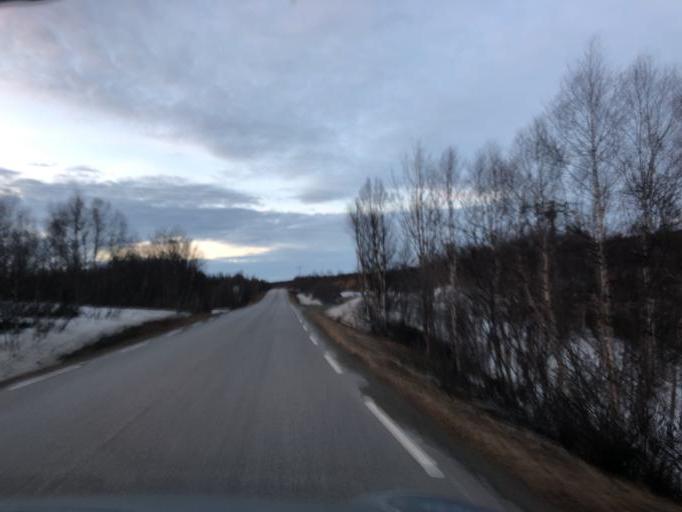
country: NO
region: Sor-Trondelag
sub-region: Tydal
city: Aas
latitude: 62.6510
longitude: 11.8652
